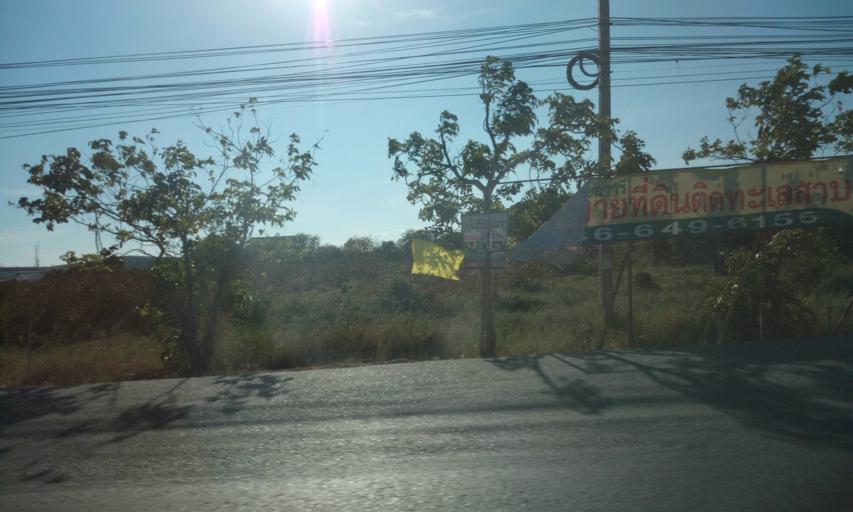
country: TH
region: Samut Prakan
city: Bang Bo District
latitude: 13.5872
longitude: 100.7594
